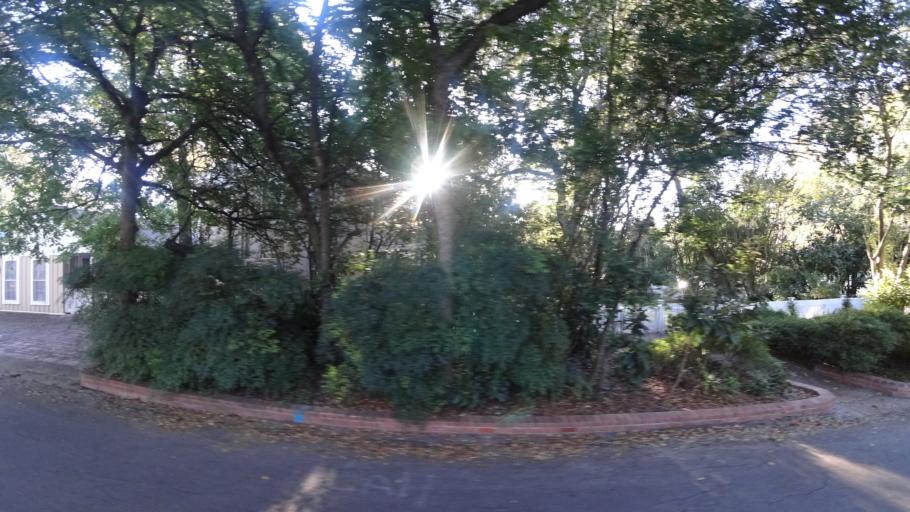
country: US
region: Texas
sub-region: Travis County
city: West Lake Hills
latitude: 30.3006
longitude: -97.7753
